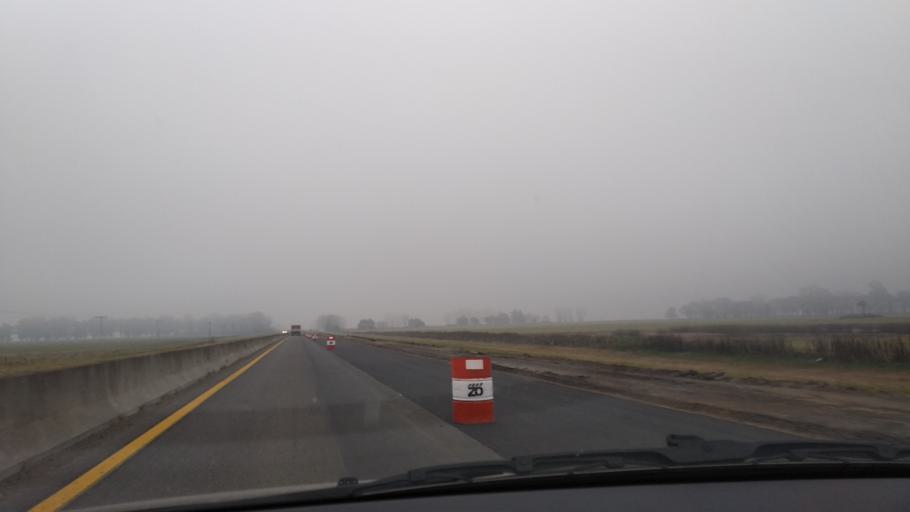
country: AR
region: Buenos Aires
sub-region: Partido de Azul
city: Azul
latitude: -36.8472
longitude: -59.9491
